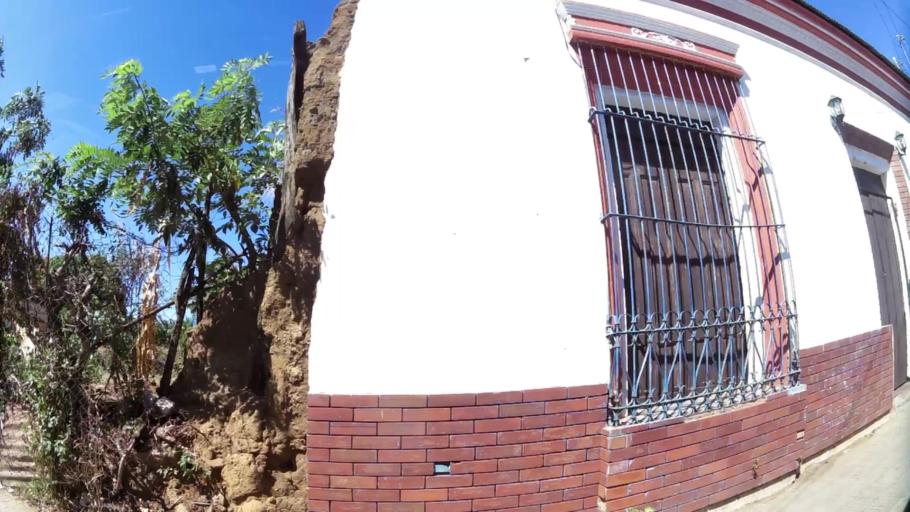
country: SV
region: Ahuachapan
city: Ahuachapan
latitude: 13.9216
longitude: -89.8458
